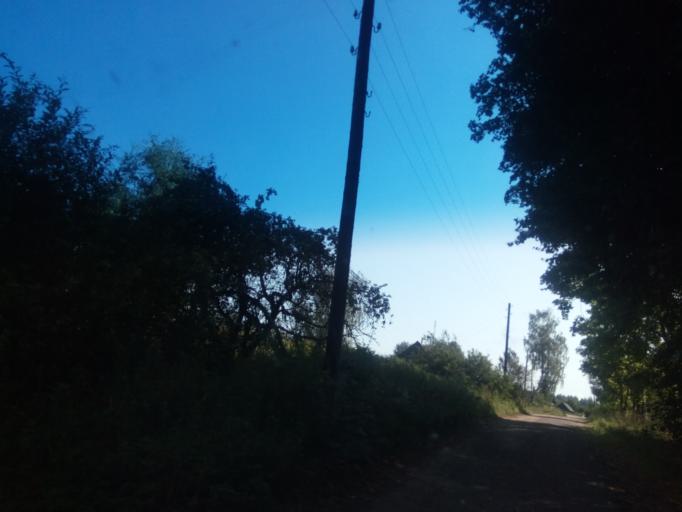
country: BY
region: Vitebsk
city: Dzisna
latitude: 55.6480
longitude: 28.2558
